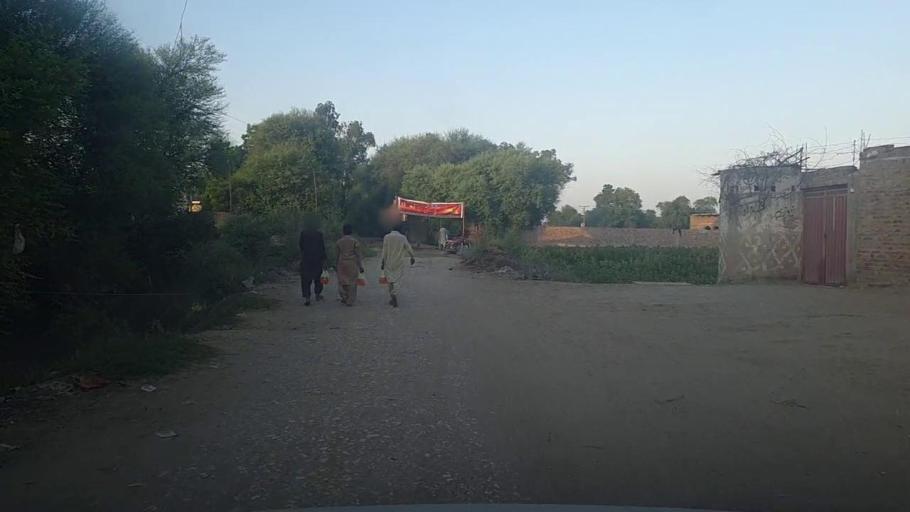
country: PK
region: Sindh
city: Khairpur
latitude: 28.0801
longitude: 69.7134
